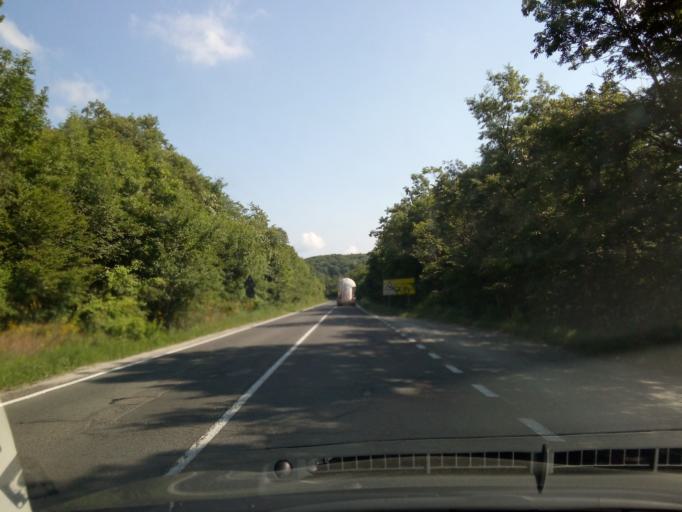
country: BG
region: Burgas
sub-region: Obshtina Nesebur
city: Sveti Vlas
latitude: 42.7603
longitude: 27.7524
